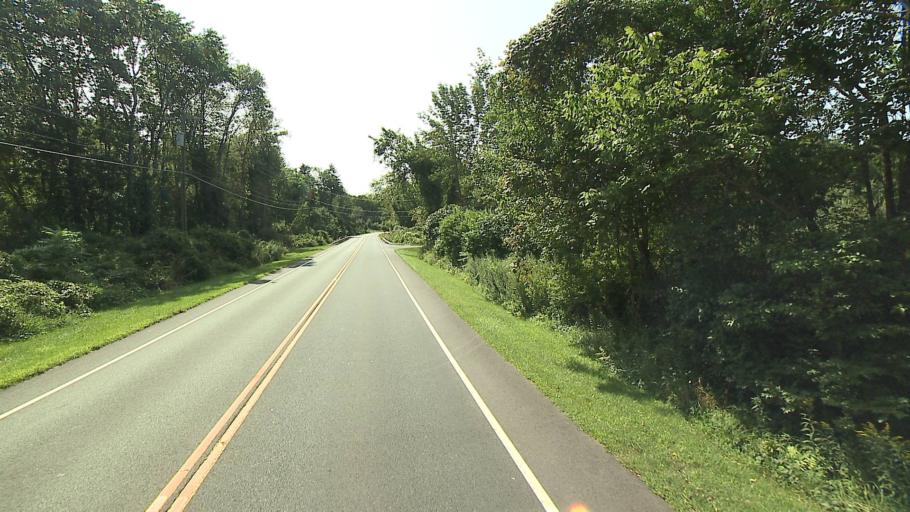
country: US
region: Connecticut
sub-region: Fairfield County
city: Newtown
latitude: 41.4331
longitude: -73.3553
